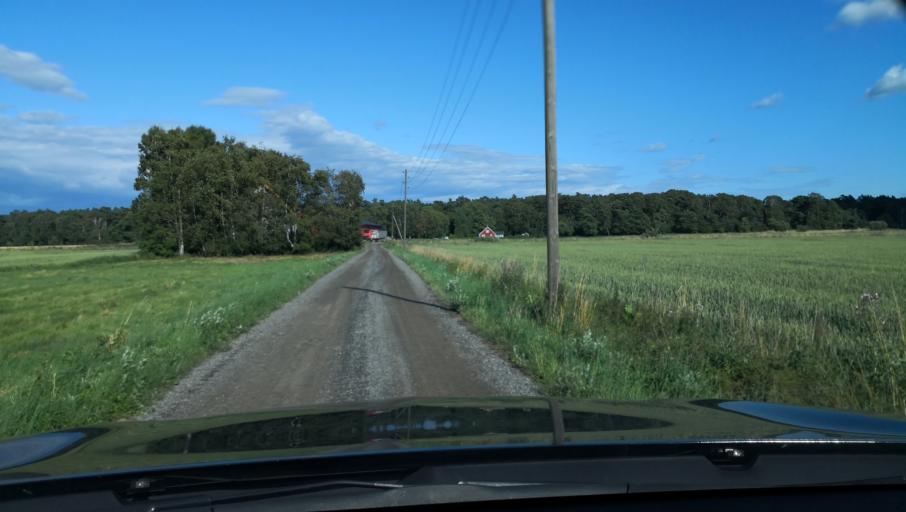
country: SE
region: Skane
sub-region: Kristianstads Kommun
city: Degeberga
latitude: 55.8084
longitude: 14.1905
